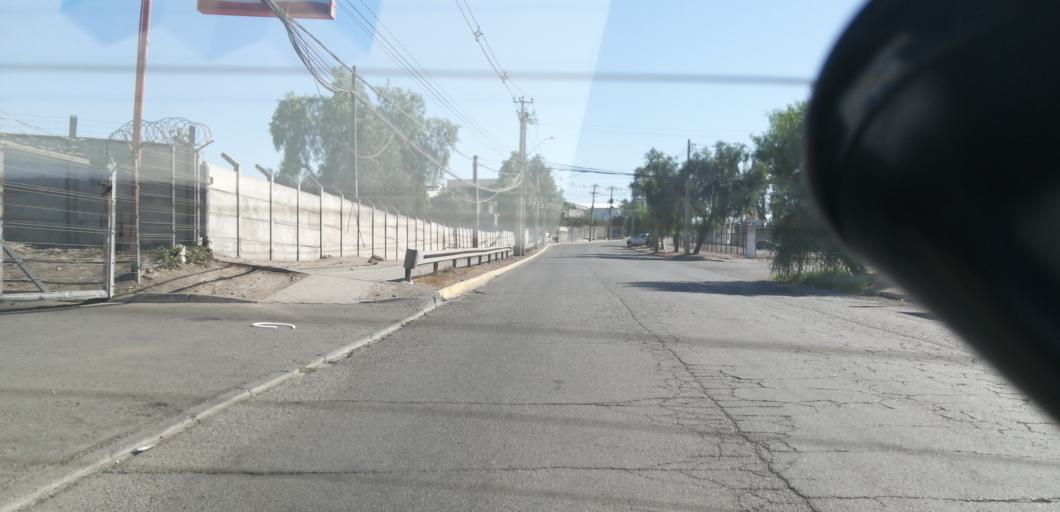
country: CL
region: Santiago Metropolitan
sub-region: Provincia de Santiago
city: Lo Prado
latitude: -33.4494
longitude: -70.7843
